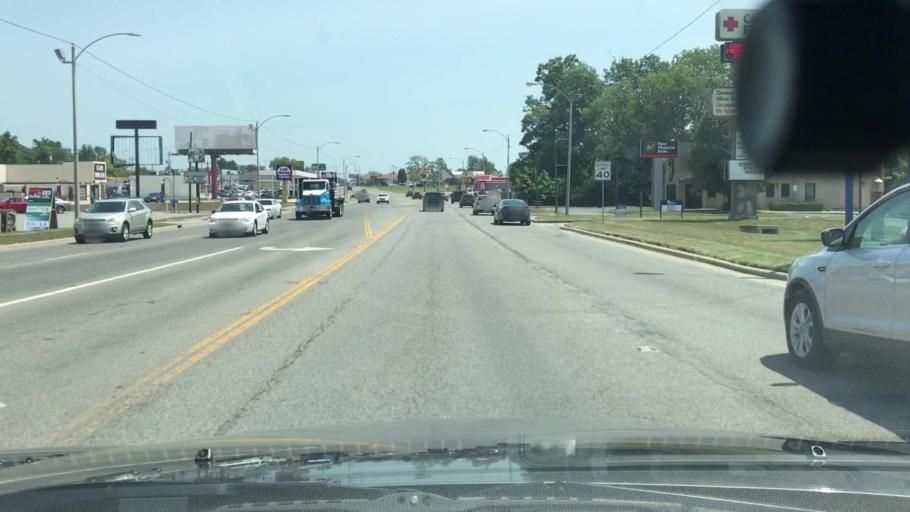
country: US
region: Illinois
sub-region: Jefferson County
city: Mount Vernon
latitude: 38.3143
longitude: -88.9332
